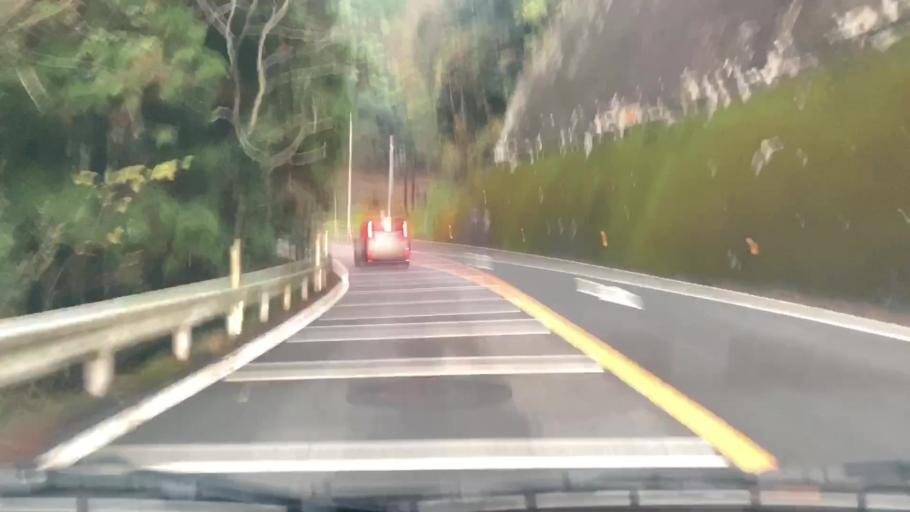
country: JP
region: Saga Prefecture
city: Ureshinomachi-shimojuku
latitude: 33.0599
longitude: 129.9497
